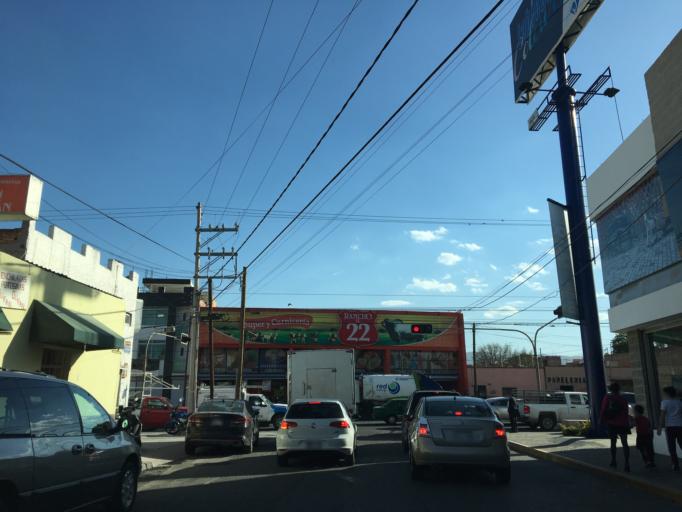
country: MX
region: San Luis Potosi
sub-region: San Luis Potosi
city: San Luis Potosi
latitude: 22.1448
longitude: -100.9923
